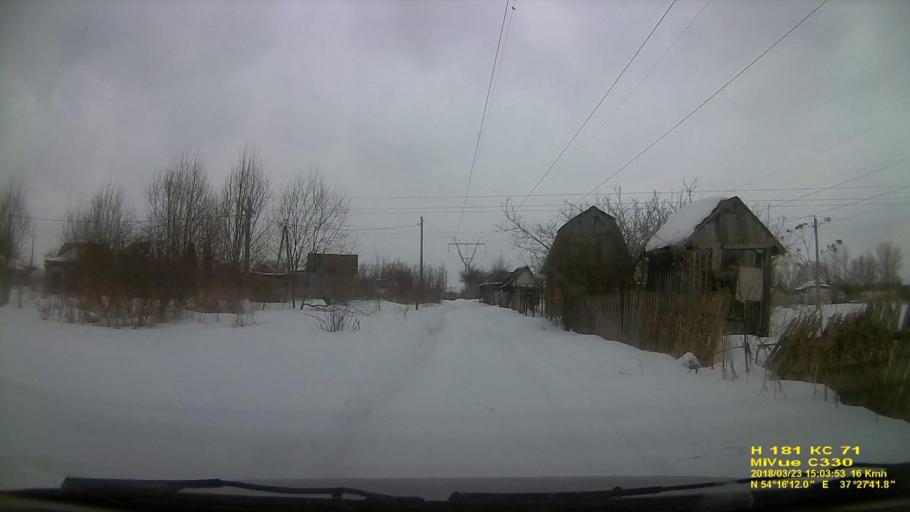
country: RU
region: Tula
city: Leninskiy
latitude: 54.2701
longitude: 37.4616
